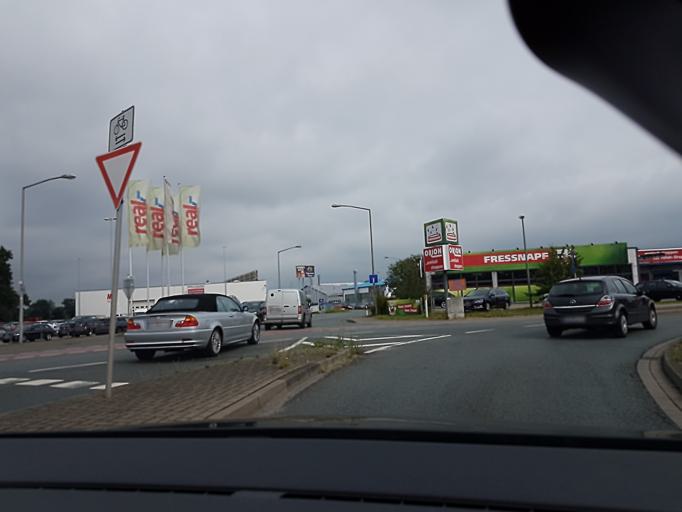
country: DE
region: Lower Saxony
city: Stuhr
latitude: 53.0120
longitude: 8.7050
